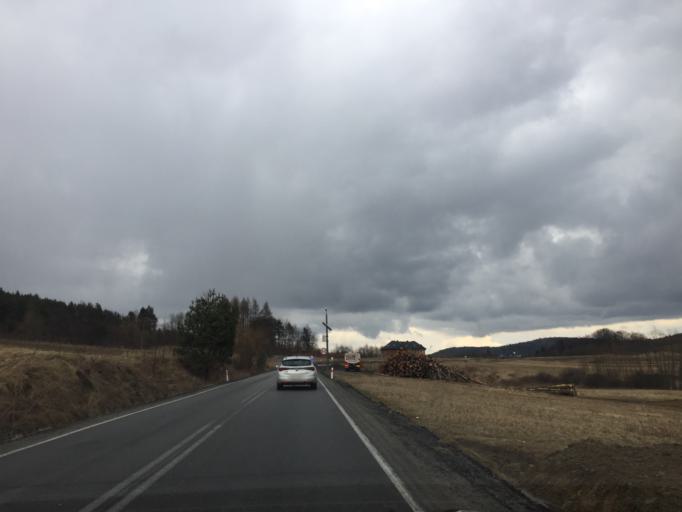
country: PL
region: Lesser Poland Voivodeship
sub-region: Powiat suski
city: Palcza
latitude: 49.8066
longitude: 19.7522
